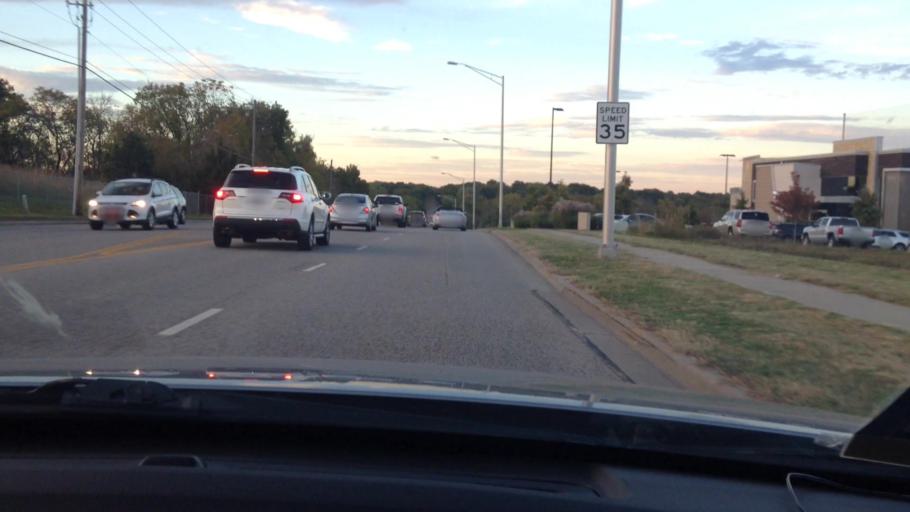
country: US
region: Kansas
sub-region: Johnson County
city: Leawood
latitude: 38.9334
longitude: -94.6486
